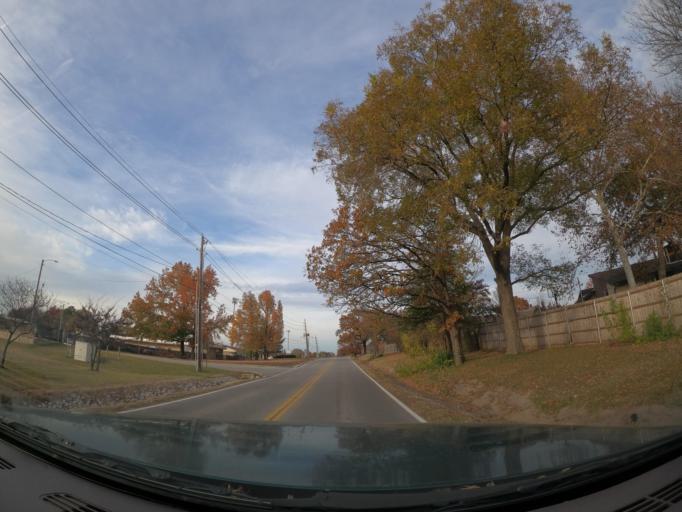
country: US
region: Oklahoma
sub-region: Tulsa County
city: Jenks
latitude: 36.0427
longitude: -95.9400
